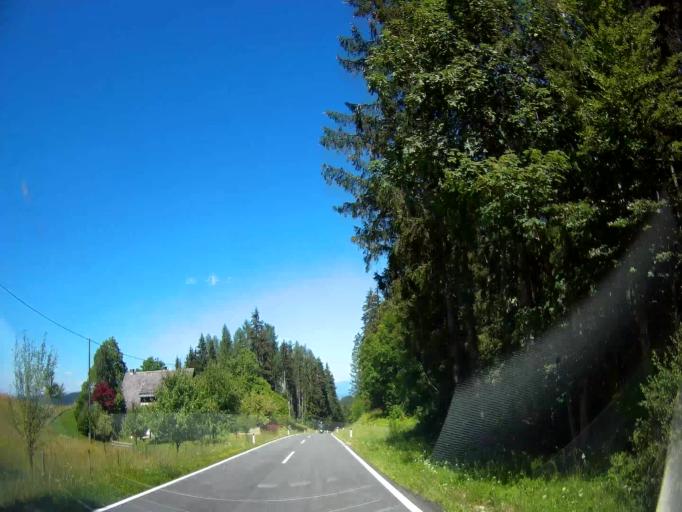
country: AT
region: Carinthia
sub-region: Politischer Bezirk Volkermarkt
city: Gallizien
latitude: 46.5374
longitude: 14.4692
